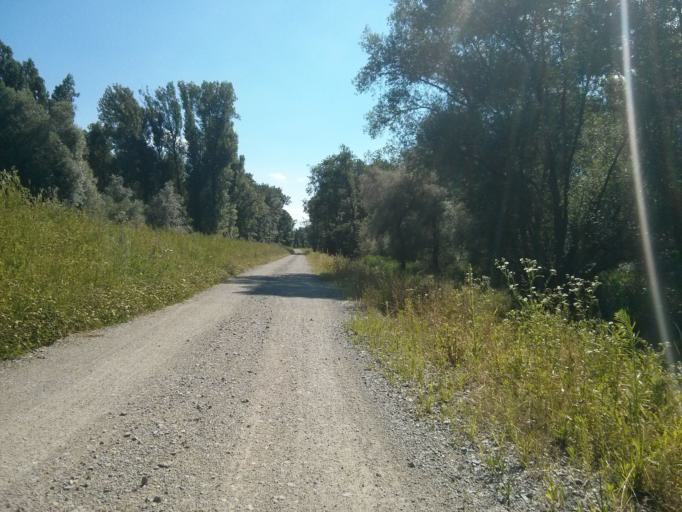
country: DE
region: Bavaria
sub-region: Lower Bavaria
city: Deggendorf
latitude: 48.7994
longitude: 12.9596
